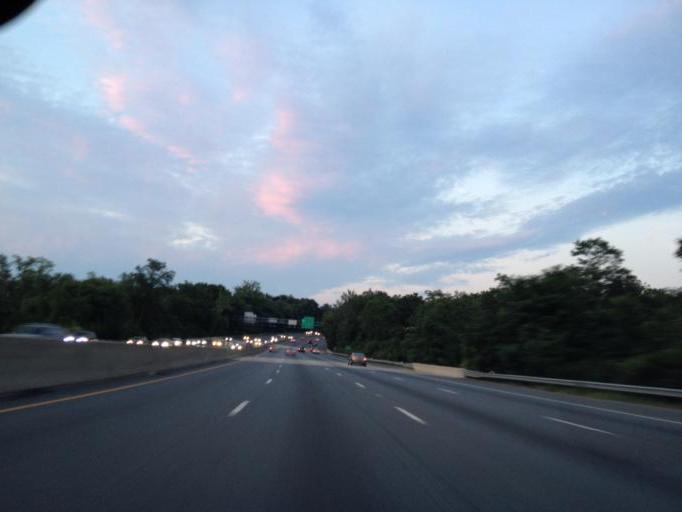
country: US
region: Maryland
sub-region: Montgomery County
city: Forest Glen
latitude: 39.0140
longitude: -77.0337
